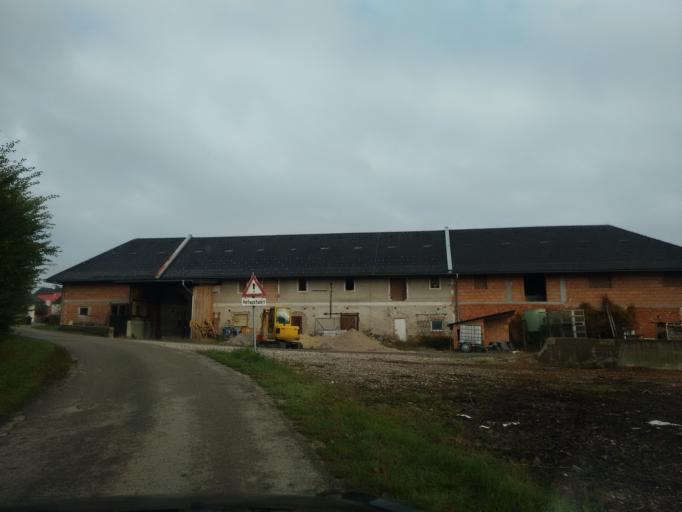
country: AT
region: Upper Austria
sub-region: Wels-Land
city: Gunskirchen
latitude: 48.1914
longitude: 13.9703
